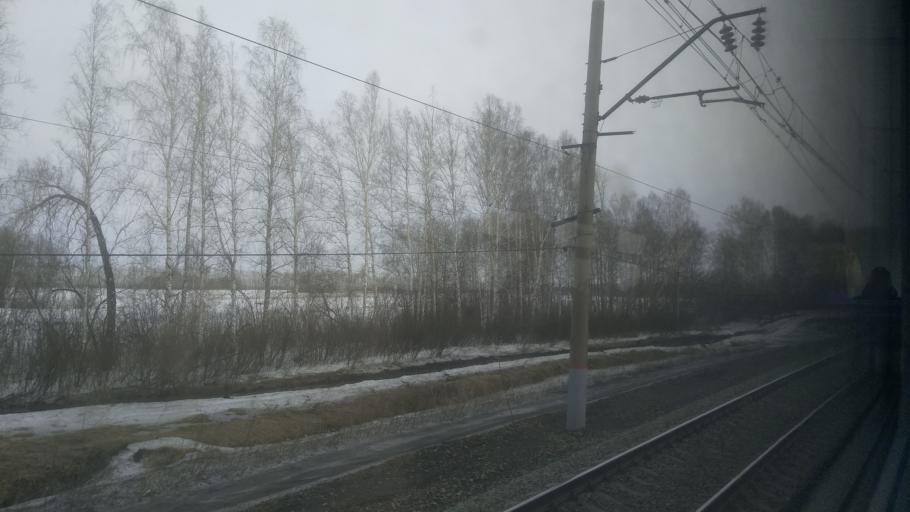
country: RU
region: Novosibirsk
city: Bolotnoye
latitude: 55.7089
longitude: 84.6127
